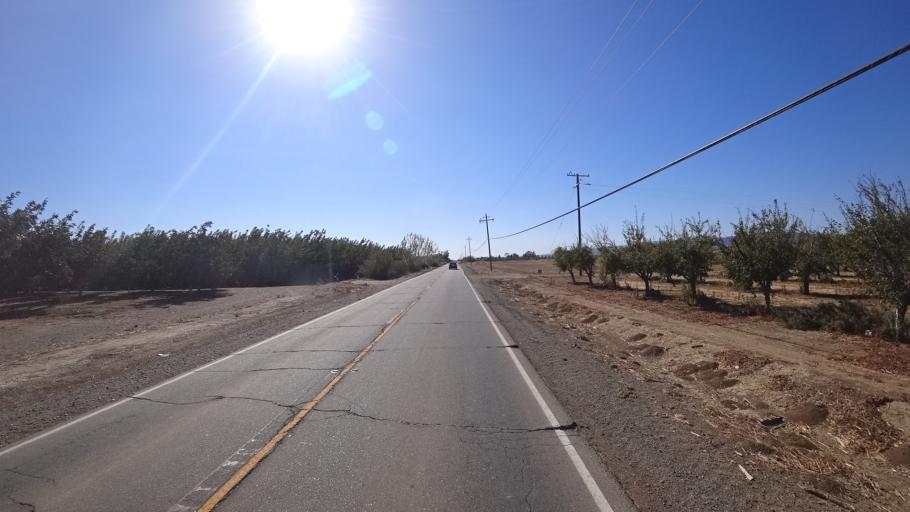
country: US
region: California
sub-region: Yolo County
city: Winters
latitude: 38.5773
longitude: -121.9714
